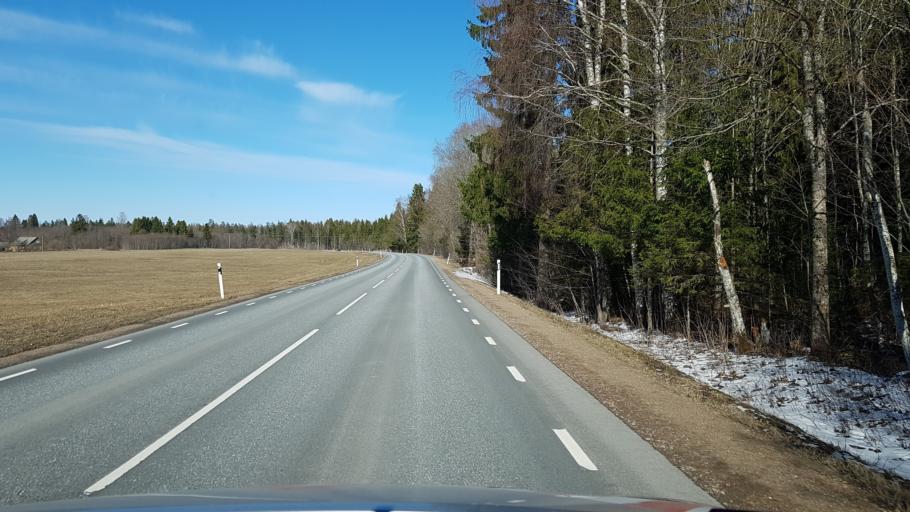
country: EE
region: Laeaene-Virumaa
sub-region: Tapa vald
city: Tapa
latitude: 59.3807
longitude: 26.0111
